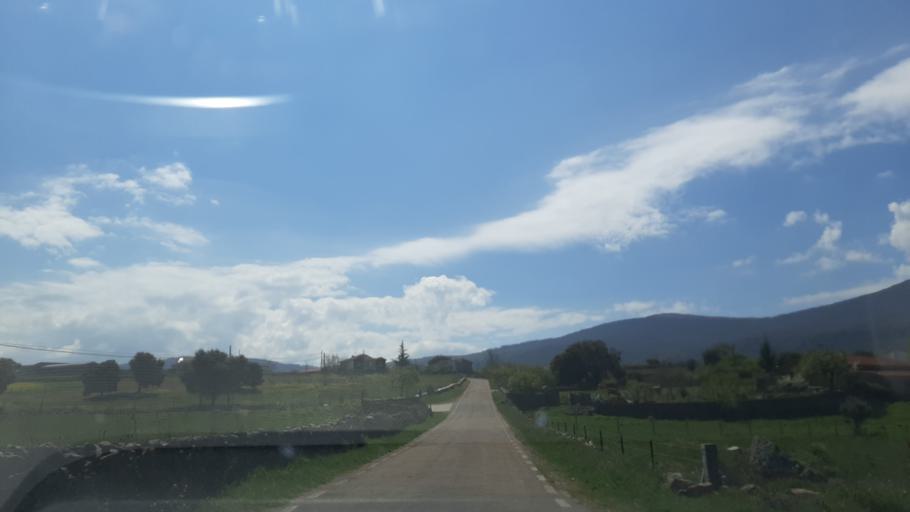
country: ES
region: Castille and Leon
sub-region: Provincia de Salamanca
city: Navarredonda de la Rinconada
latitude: 40.6164
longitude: -6.0196
